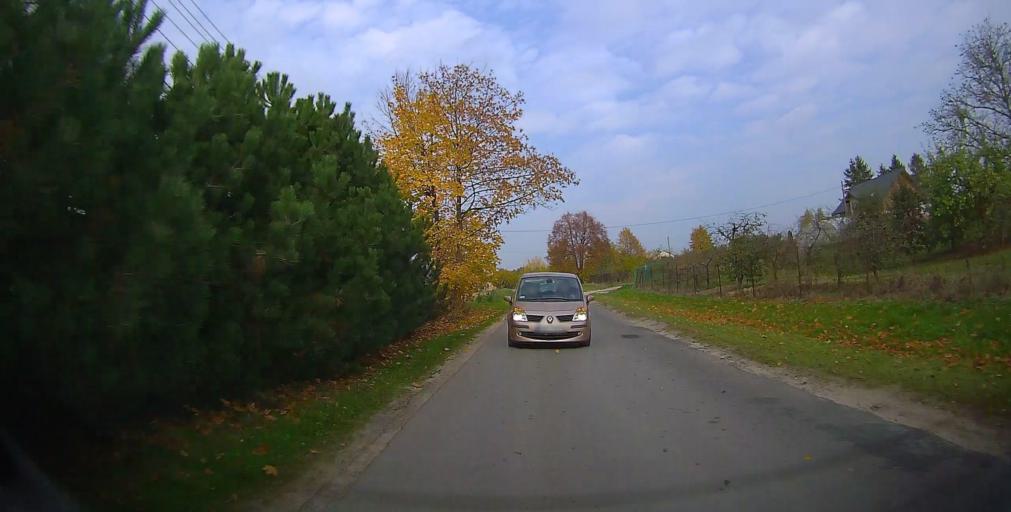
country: PL
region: Masovian Voivodeship
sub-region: Powiat grojecki
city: Mogielnica
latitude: 51.6459
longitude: 20.7347
